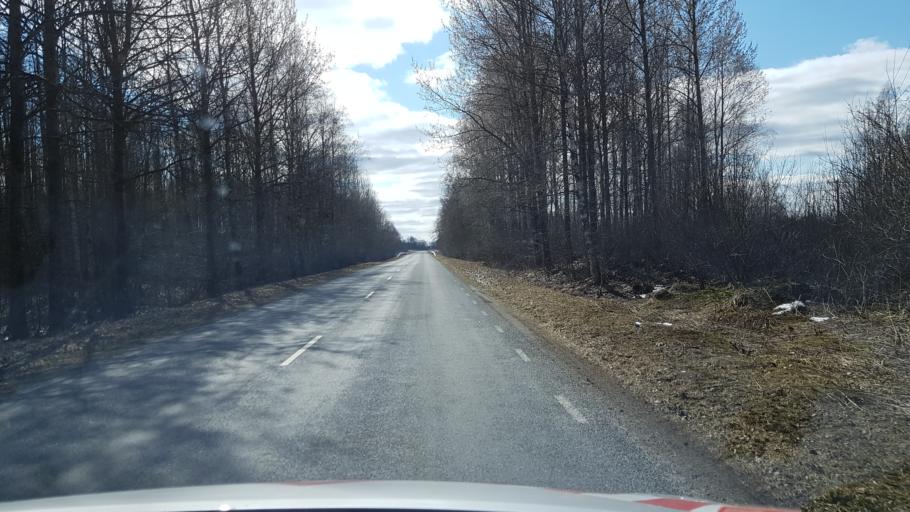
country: EE
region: Laeaene-Virumaa
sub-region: Tapa vald
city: Tapa
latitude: 59.2623
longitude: 25.8465
